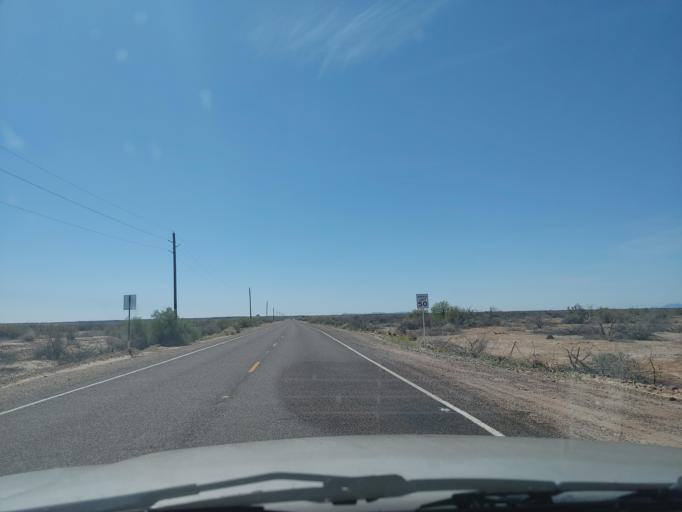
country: US
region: Arizona
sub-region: Maricopa County
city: Gila Bend
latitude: 32.9721
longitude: -113.3060
